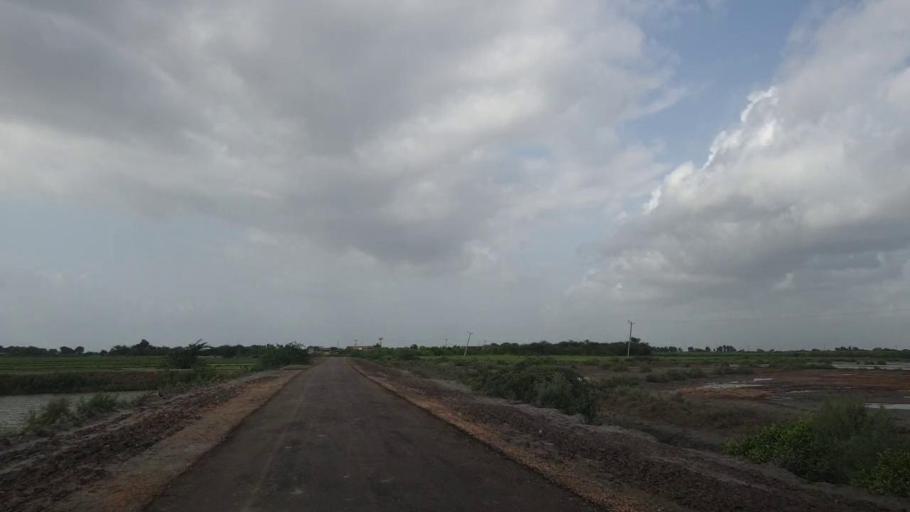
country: PK
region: Sindh
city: Kadhan
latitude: 24.5932
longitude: 69.0557
